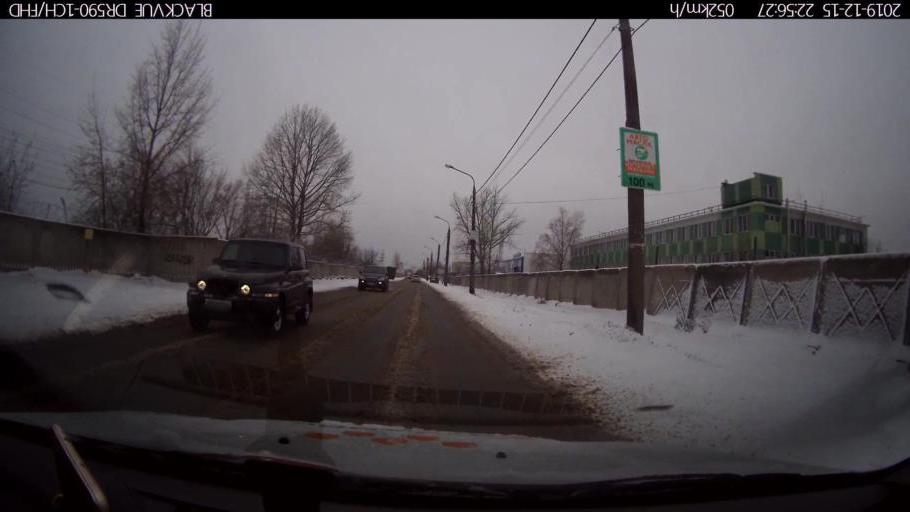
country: RU
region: Nizjnij Novgorod
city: Neklyudovo
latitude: 56.3499
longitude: 43.8934
